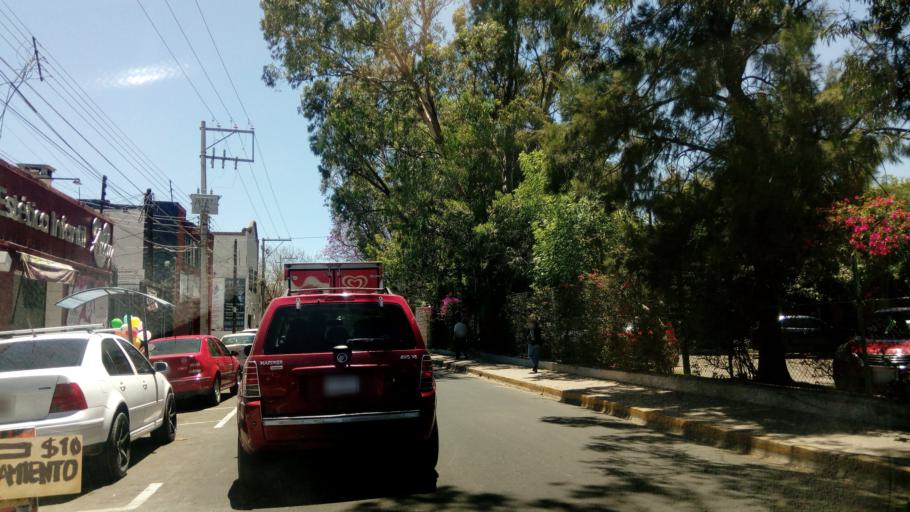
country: MX
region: Durango
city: Victoria de Durango
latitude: 24.0274
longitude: -104.6614
